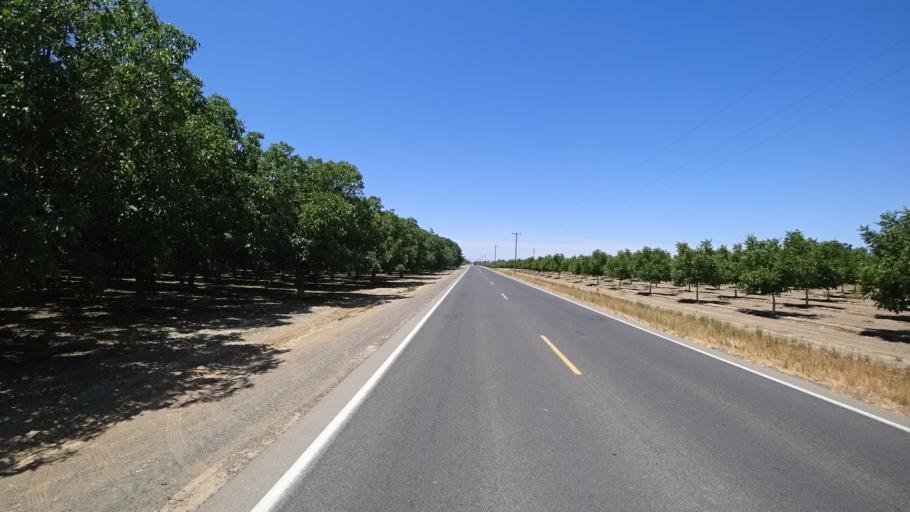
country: US
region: California
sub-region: Kings County
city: Lemoore
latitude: 36.3426
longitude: -119.7652
